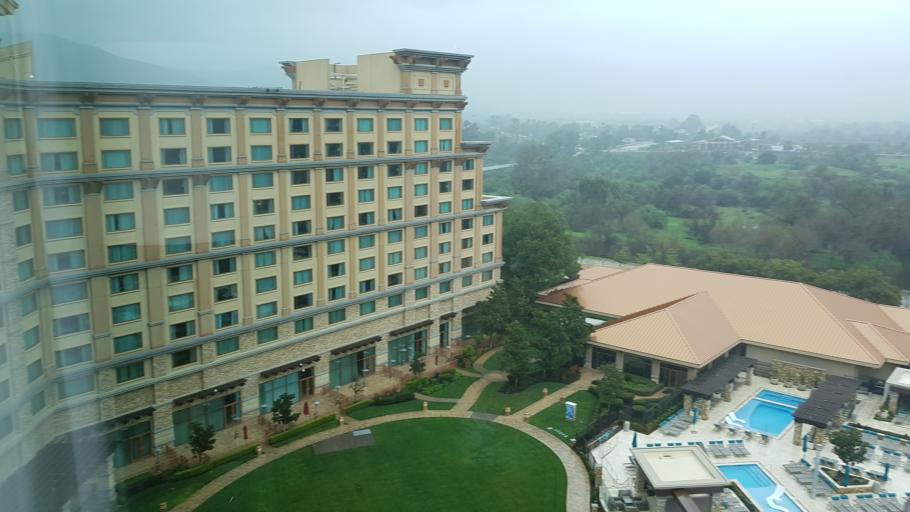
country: US
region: California
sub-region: San Diego County
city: Rainbow
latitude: 33.3629
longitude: -117.0831
